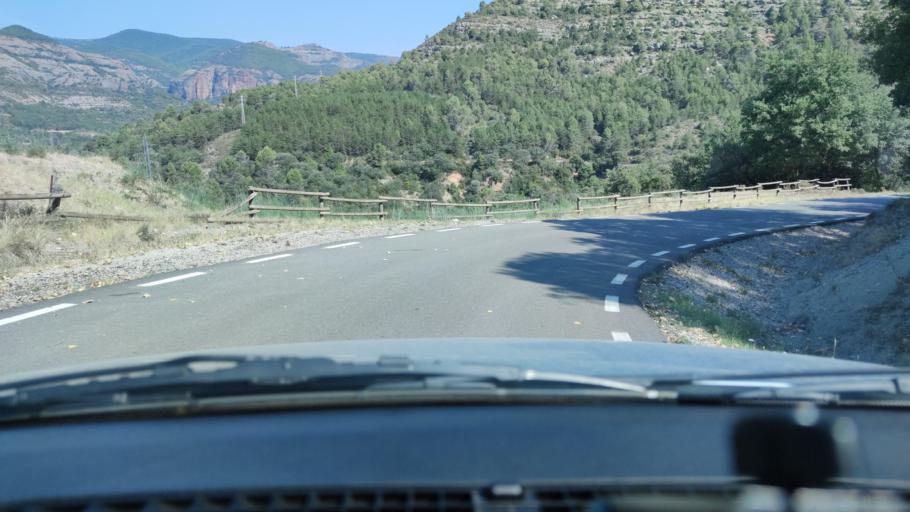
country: ES
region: Catalonia
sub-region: Provincia de Lleida
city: Senterada
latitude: 42.2742
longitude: 0.9507
